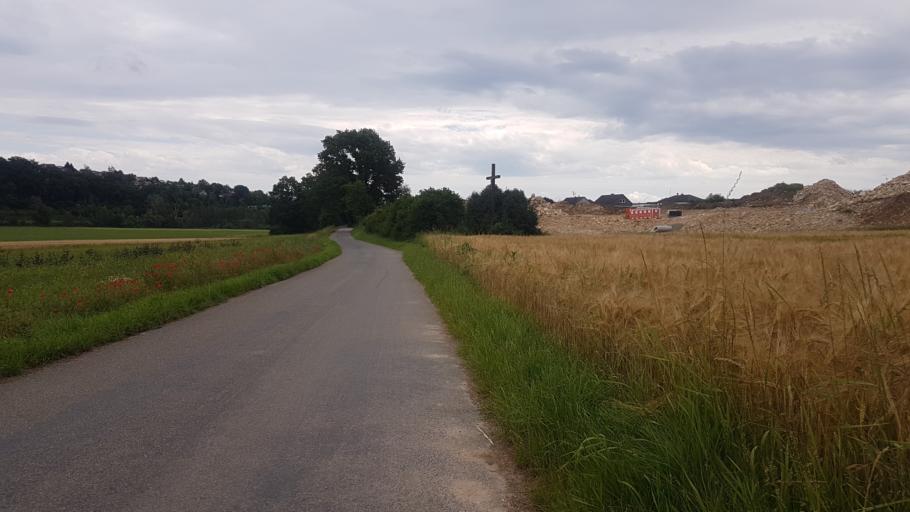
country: DE
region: Baden-Wuerttemberg
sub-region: Tuebingen Region
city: Sigmaringendorf
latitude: 48.0707
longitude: 9.2493
